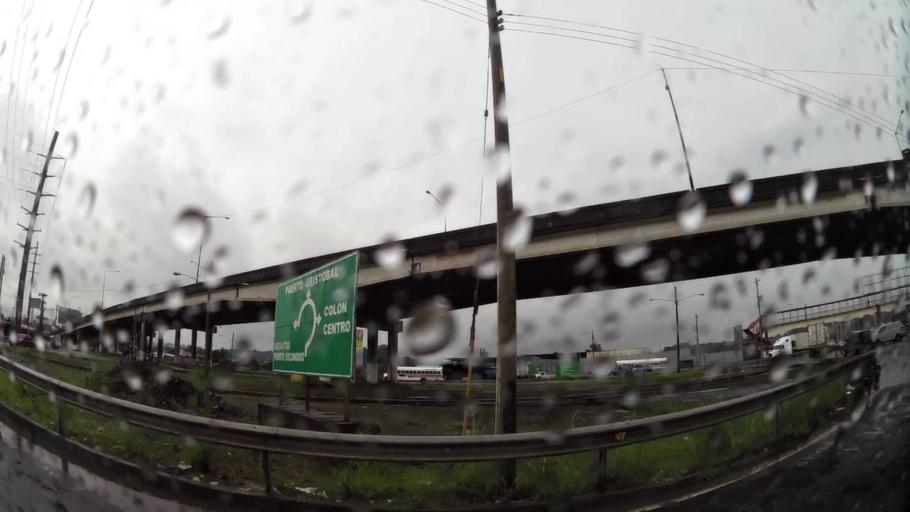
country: PA
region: Colon
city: Arco Iris
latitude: 9.3398
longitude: -79.8806
